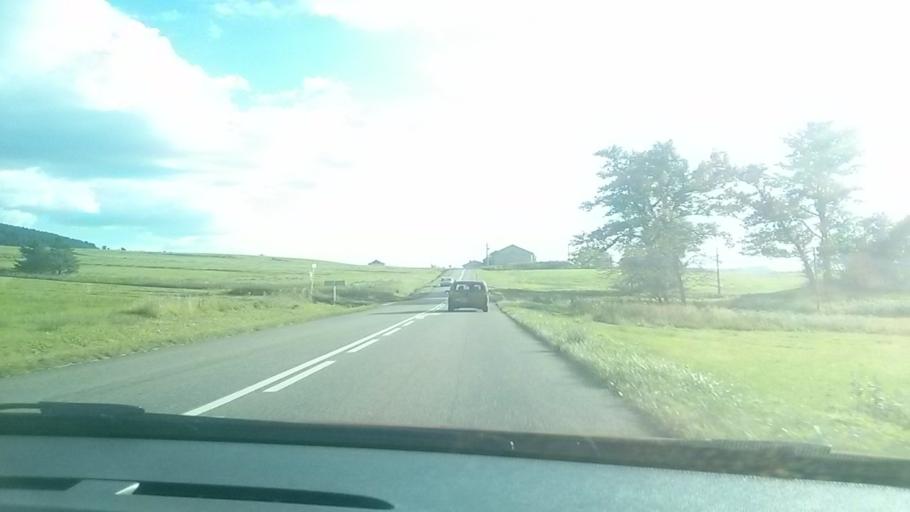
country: FR
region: Franche-Comte
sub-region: Departement du Jura
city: Les Rousses
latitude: 46.5077
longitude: 6.1074
